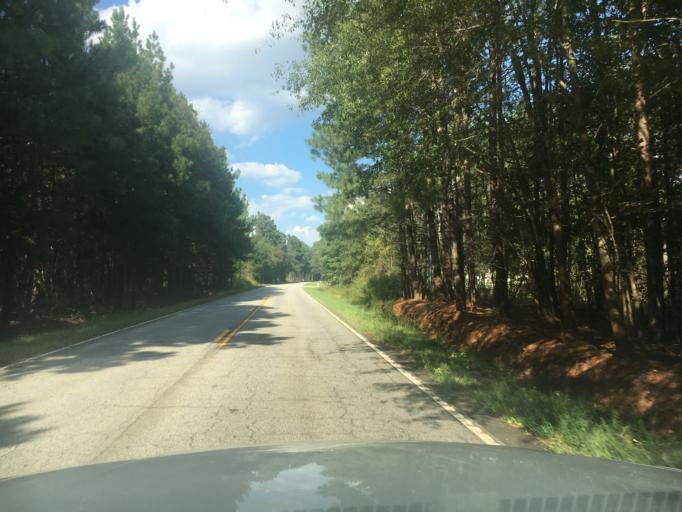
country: US
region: South Carolina
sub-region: Anderson County
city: Pendleton
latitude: 34.6737
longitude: -82.7584
